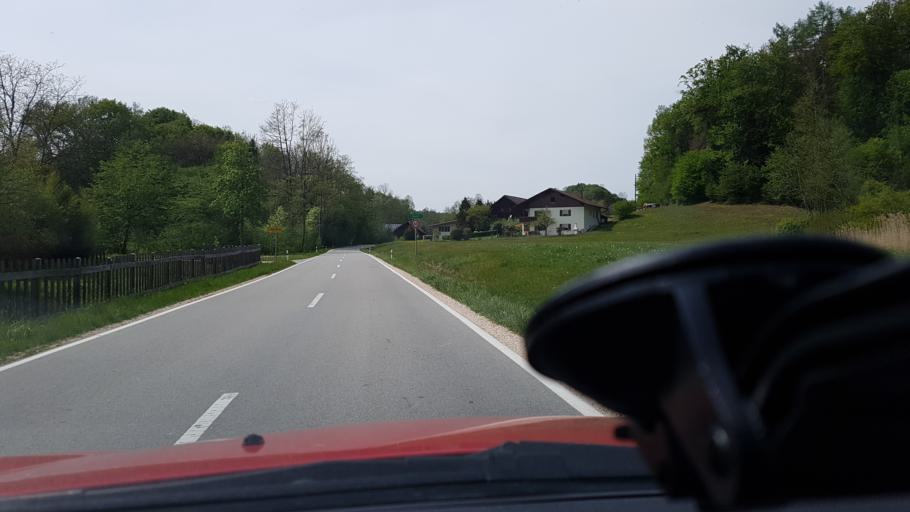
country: DE
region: Bavaria
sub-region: Lower Bavaria
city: Stubenberg
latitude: 48.3333
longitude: 13.1019
